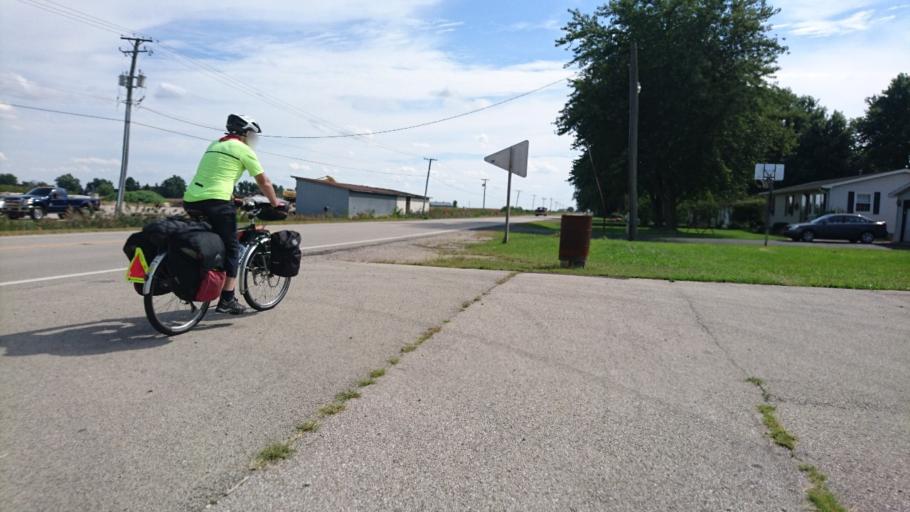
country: US
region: Illinois
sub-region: Grundy County
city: Gardner
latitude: 41.1899
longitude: -88.3014
